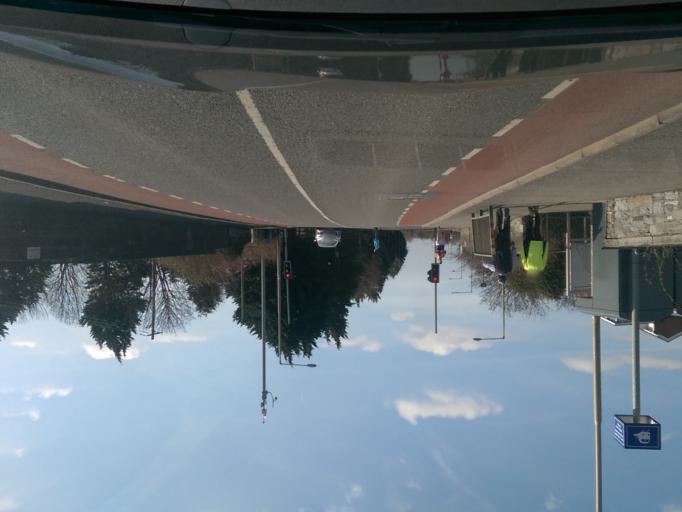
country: IE
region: Leinster
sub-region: Kildare
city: Leixlip
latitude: 53.3698
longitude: -6.5076
